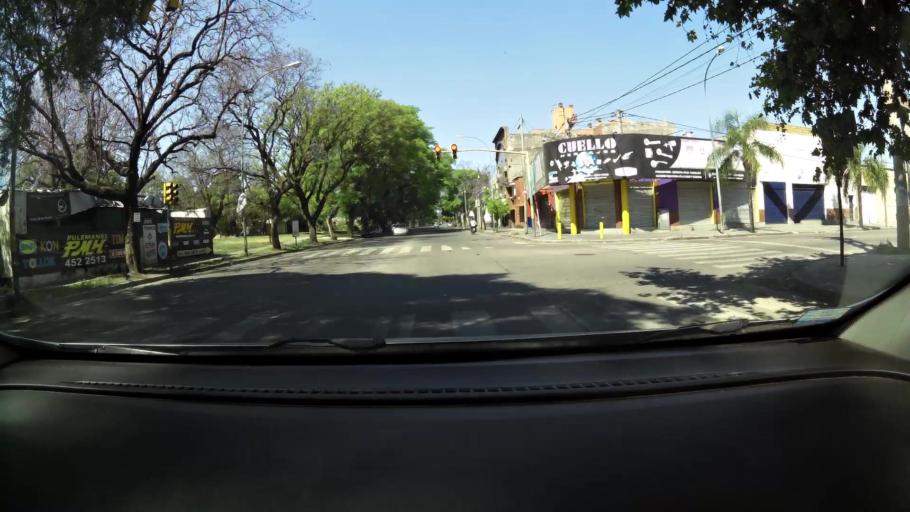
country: AR
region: Cordoba
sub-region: Departamento de Capital
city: Cordoba
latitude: -31.3990
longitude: -64.1689
